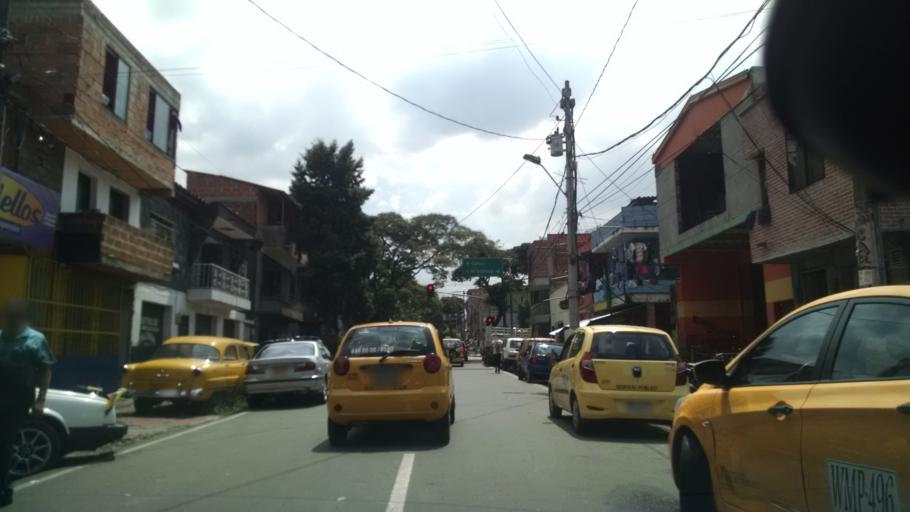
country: CO
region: Antioquia
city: Medellin
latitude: 6.2643
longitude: -75.5604
